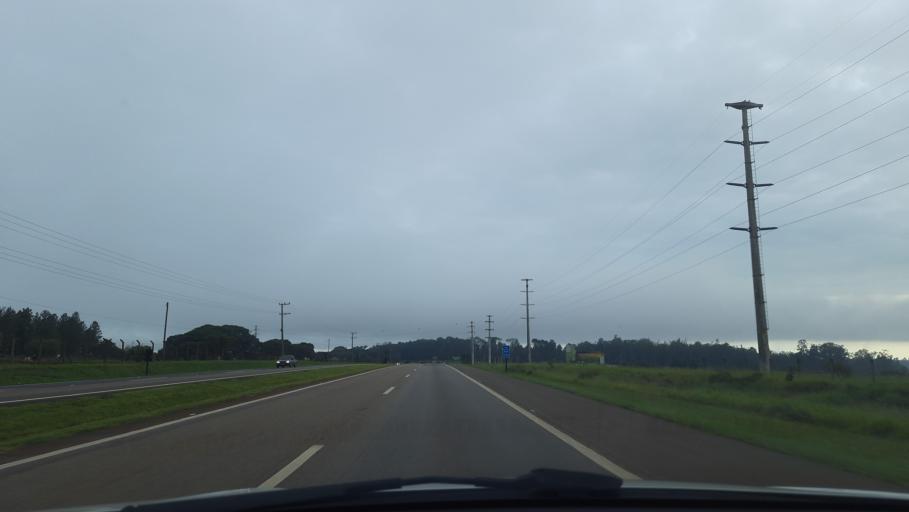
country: BR
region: Sao Paulo
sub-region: Casa Branca
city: Casa Branca
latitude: -21.7582
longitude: -47.0707
